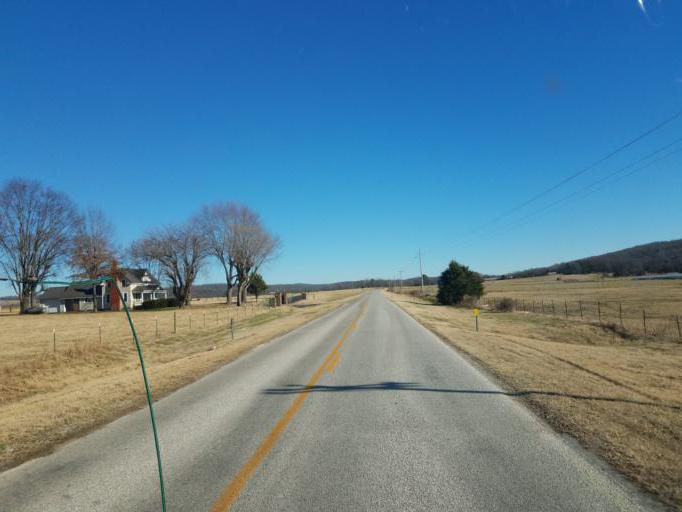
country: US
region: Arkansas
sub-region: Washington County
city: Elkins
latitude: 36.0367
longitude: -93.9650
